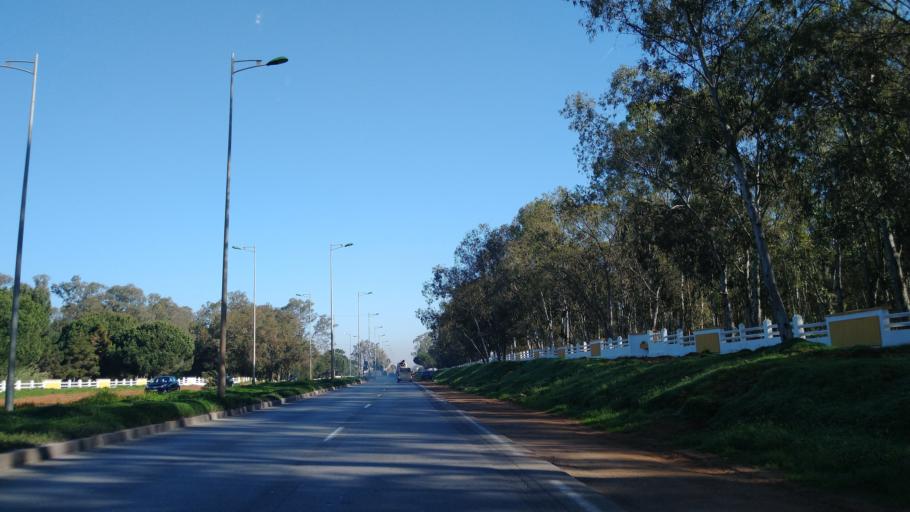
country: MA
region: Rabat-Sale-Zemmour-Zaer
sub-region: Skhirate-Temara
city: Temara
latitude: 33.9408
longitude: -6.8784
